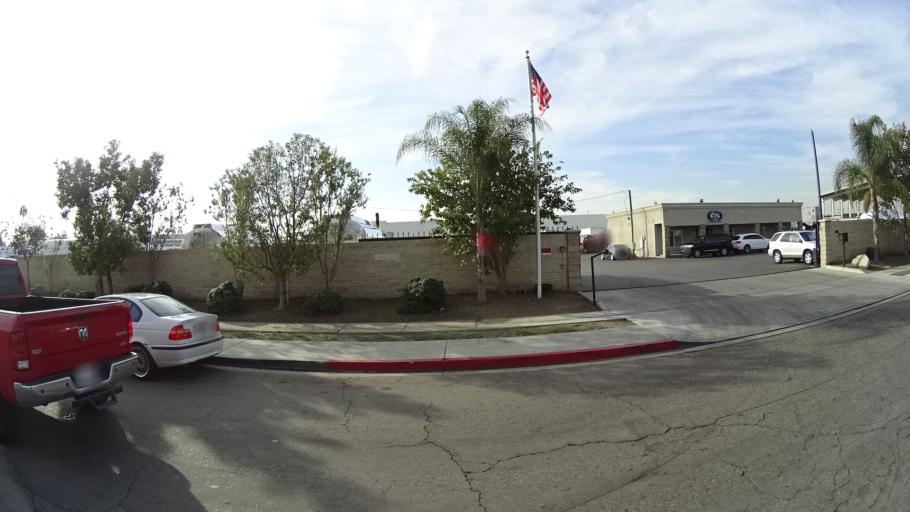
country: US
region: California
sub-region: Orange County
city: Garden Grove
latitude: 33.7604
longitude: -117.9260
